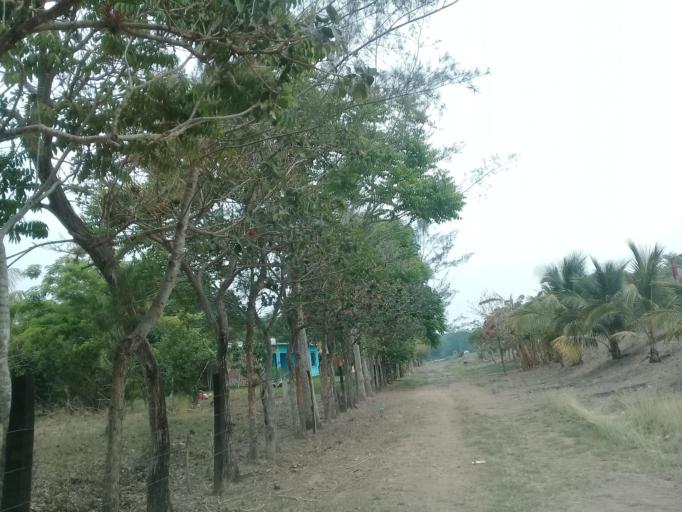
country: MX
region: Veracruz
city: Jamapa
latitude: 18.9484
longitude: -96.1978
